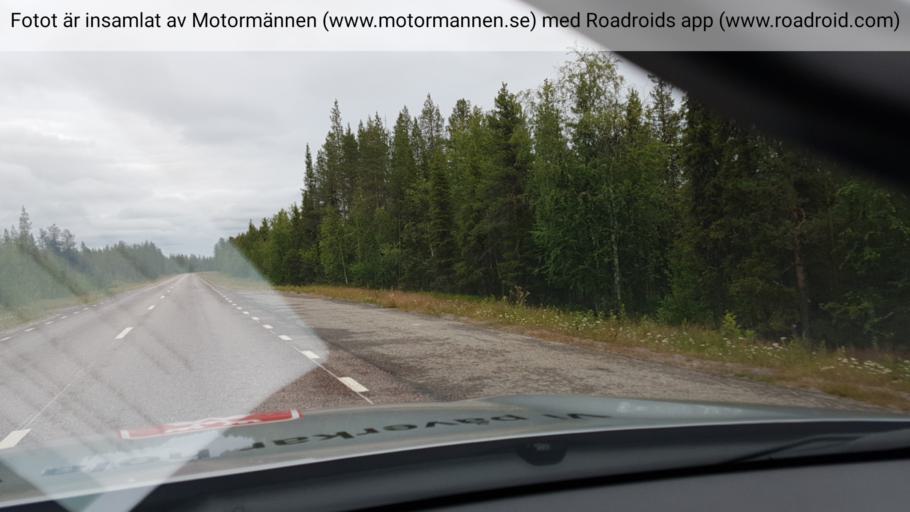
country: SE
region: Norrbotten
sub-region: Gallivare Kommun
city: Gaellivare
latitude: 67.0747
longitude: 21.4487
